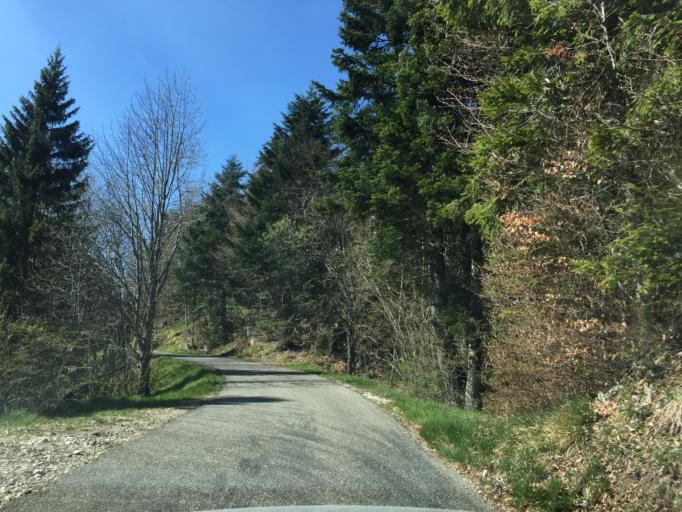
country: FR
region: Rhone-Alpes
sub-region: Departement de la Savoie
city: Novalaise
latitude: 45.6014
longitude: 5.8097
